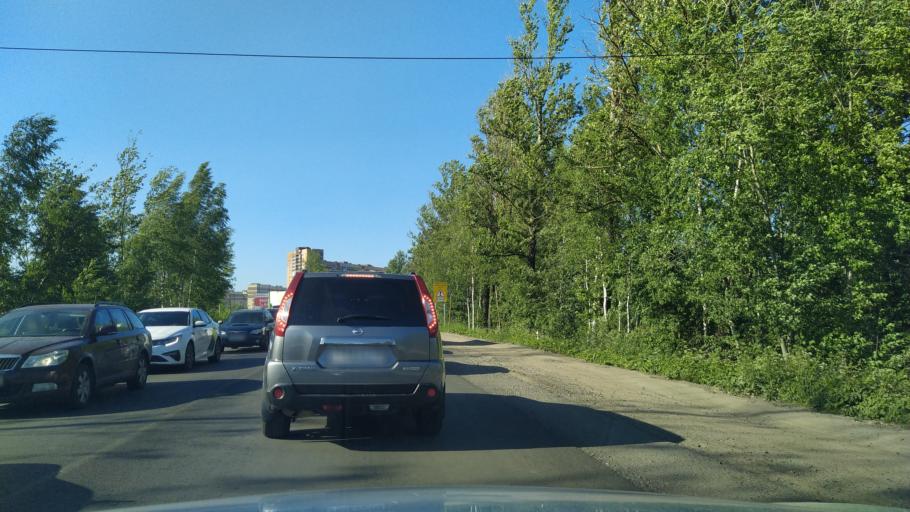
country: RU
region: Leningrad
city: Murino
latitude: 60.0504
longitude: 30.4656
